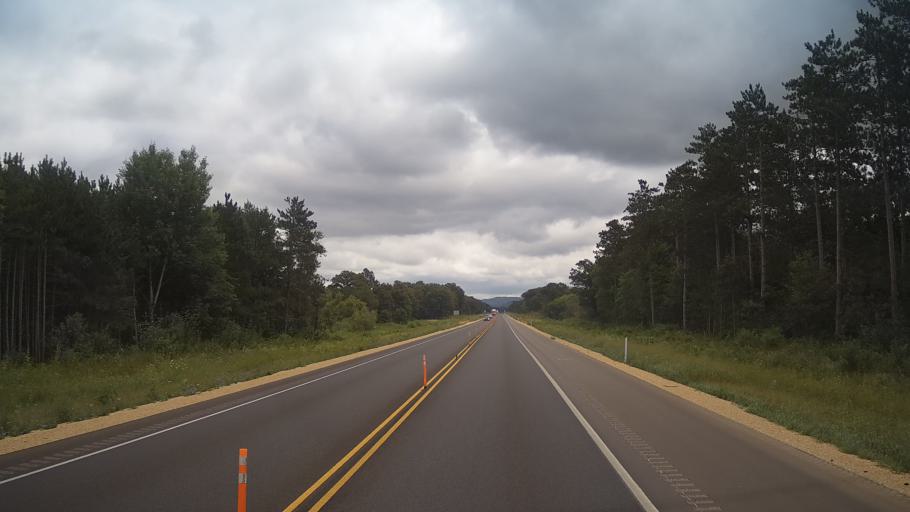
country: US
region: Wisconsin
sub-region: Monroe County
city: Sparta
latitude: 43.9430
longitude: -90.7114
